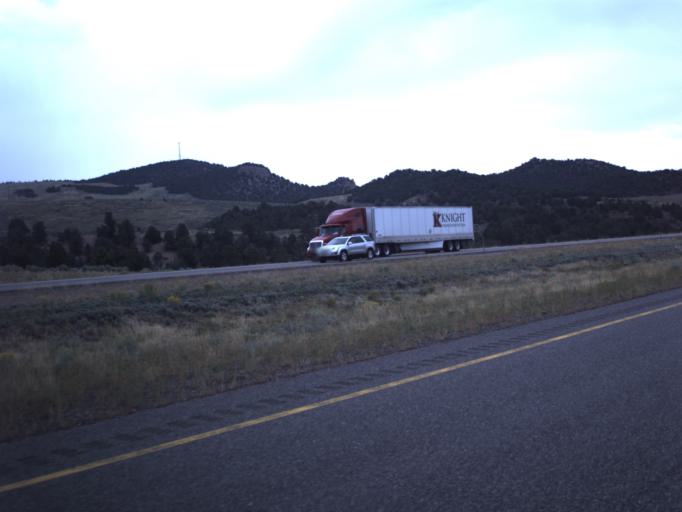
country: US
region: Utah
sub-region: Sevier County
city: Monroe
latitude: 38.5510
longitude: -112.3965
